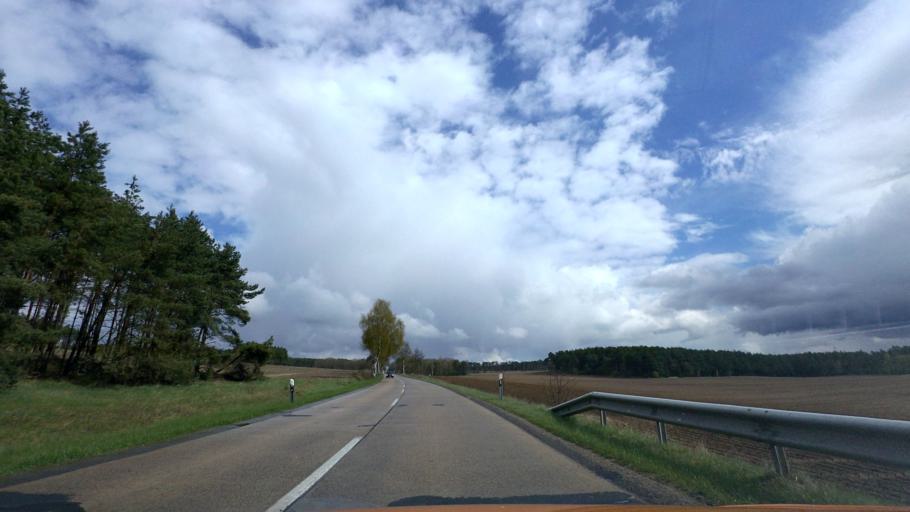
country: DE
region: Lower Saxony
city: Oldendorf
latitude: 53.1755
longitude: 10.2515
